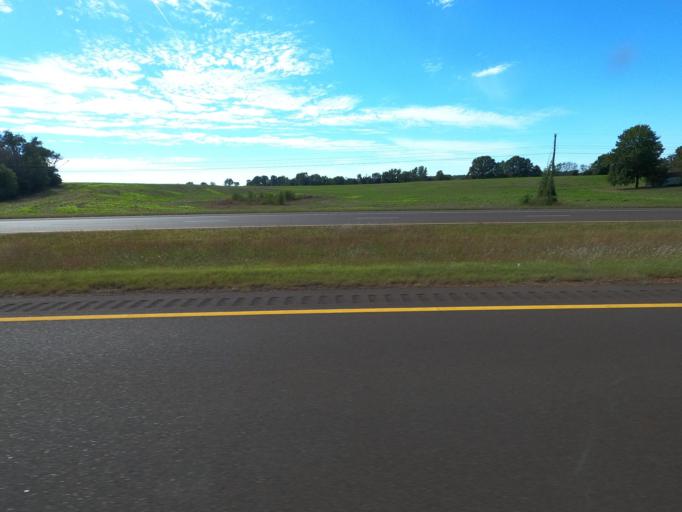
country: US
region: Tennessee
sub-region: Lauderdale County
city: Halls
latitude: 35.9174
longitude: -89.2724
